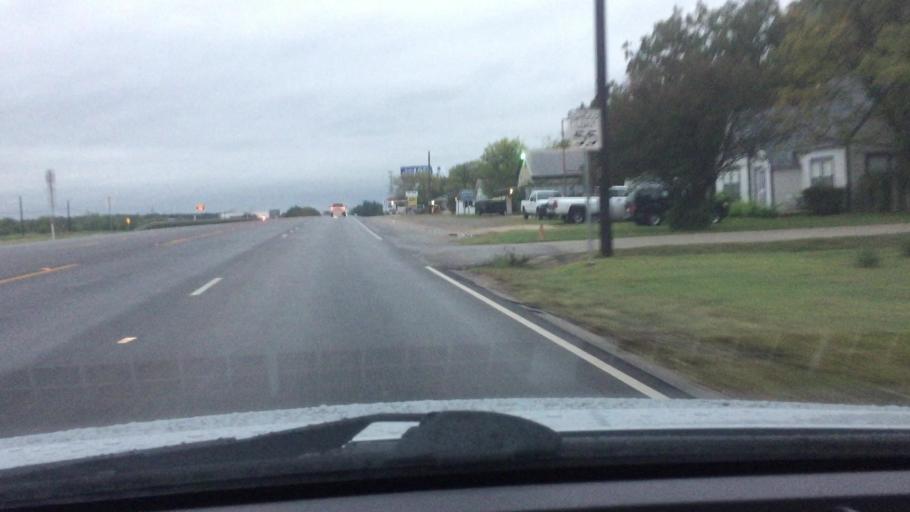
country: US
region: Texas
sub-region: Williamson County
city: Leander
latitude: 30.5779
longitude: -97.8526
